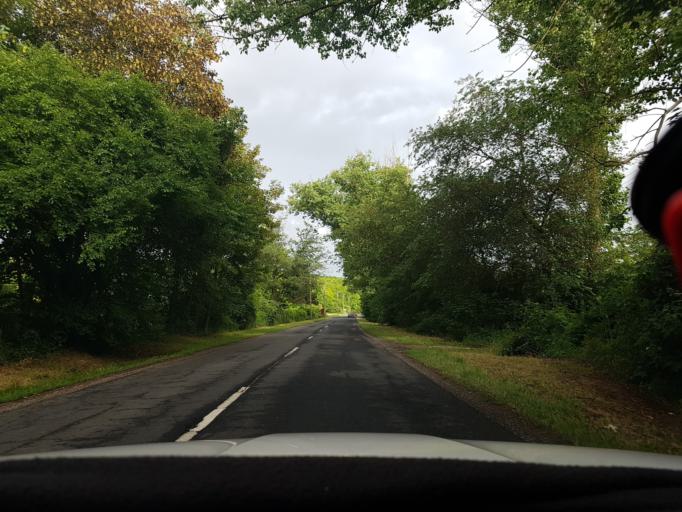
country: HU
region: Komarom-Esztergom
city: Tokod
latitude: 47.7021
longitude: 18.6526
